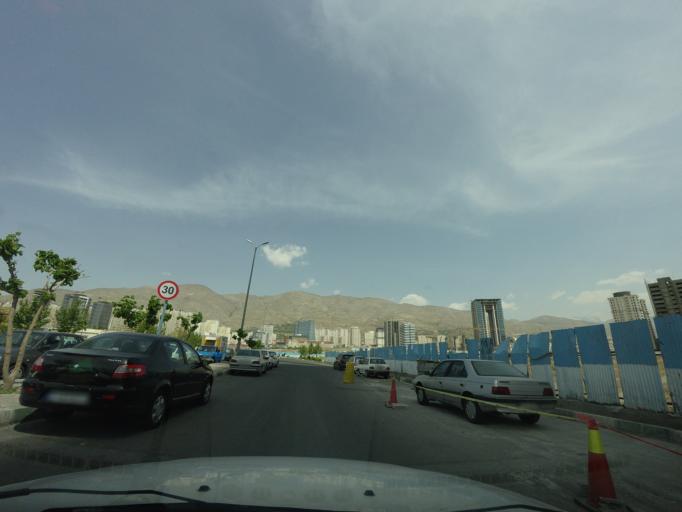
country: IR
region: Tehran
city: Shahr-e Qods
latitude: 35.7464
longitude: 51.2223
